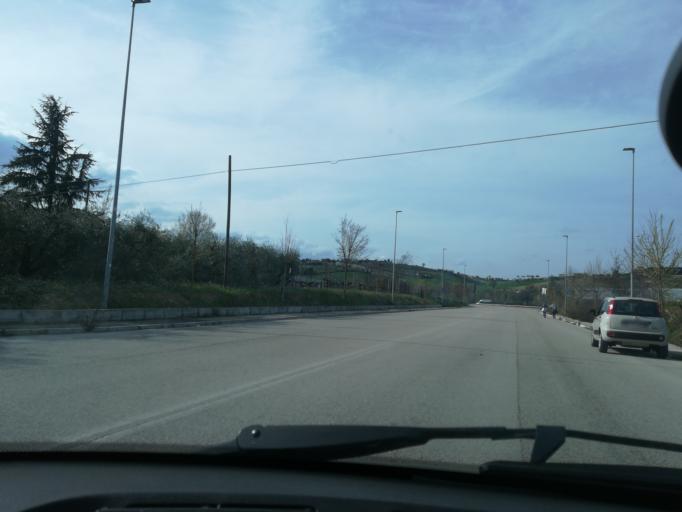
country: IT
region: The Marches
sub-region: Provincia di Macerata
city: Piediripa
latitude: 43.2813
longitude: 13.4974
